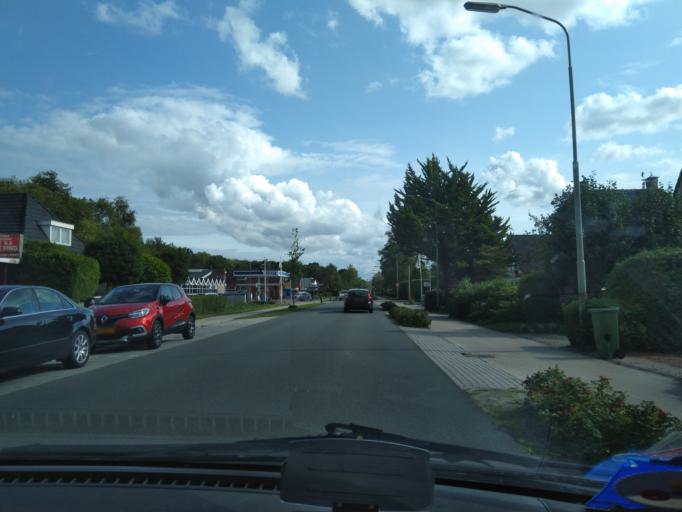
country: NL
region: Groningen
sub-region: Gemeente Groningen
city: Groningen
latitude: 53.1765
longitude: 6.5442
